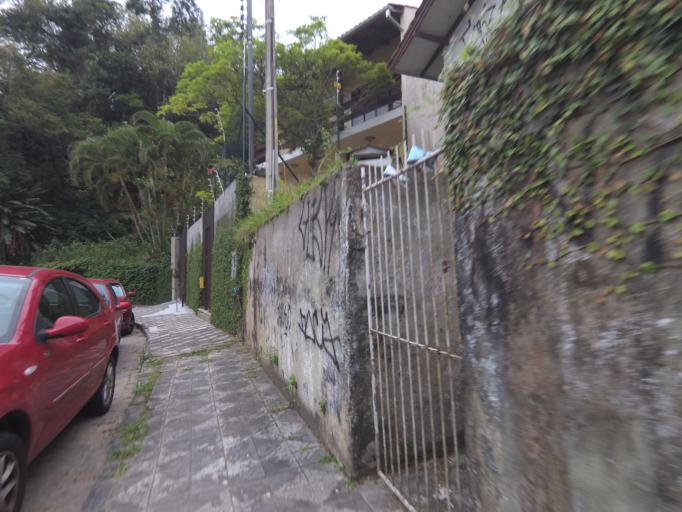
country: BR
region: Santa Catarina
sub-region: Blumenau
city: Blumenau
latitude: -26.9161
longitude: -49.0738
